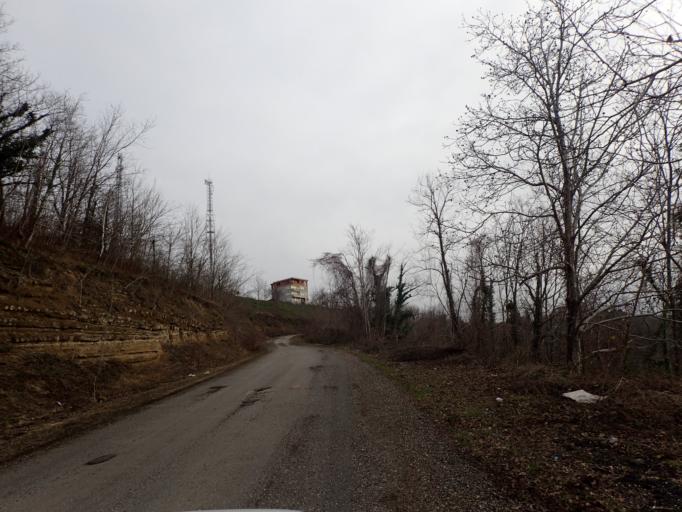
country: TR
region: Ordu
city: Camas
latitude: 40.9400
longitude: 37.5170
